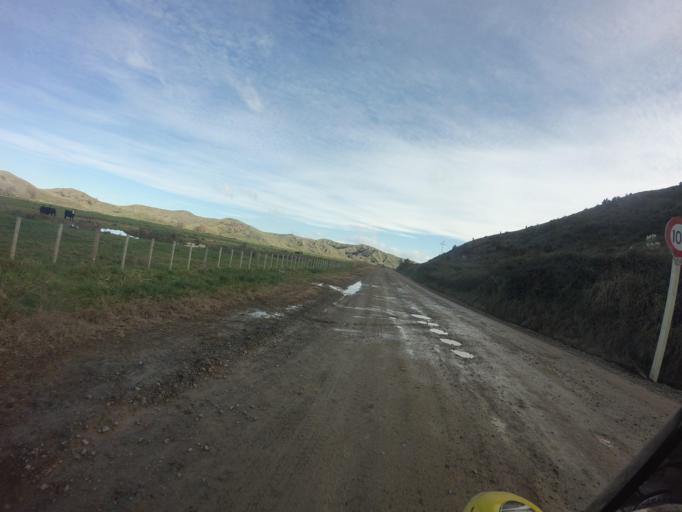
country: NZ
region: Hawke's Bay
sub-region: Wairoa District
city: Wairoa
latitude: -39.0294
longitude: 177.5882
